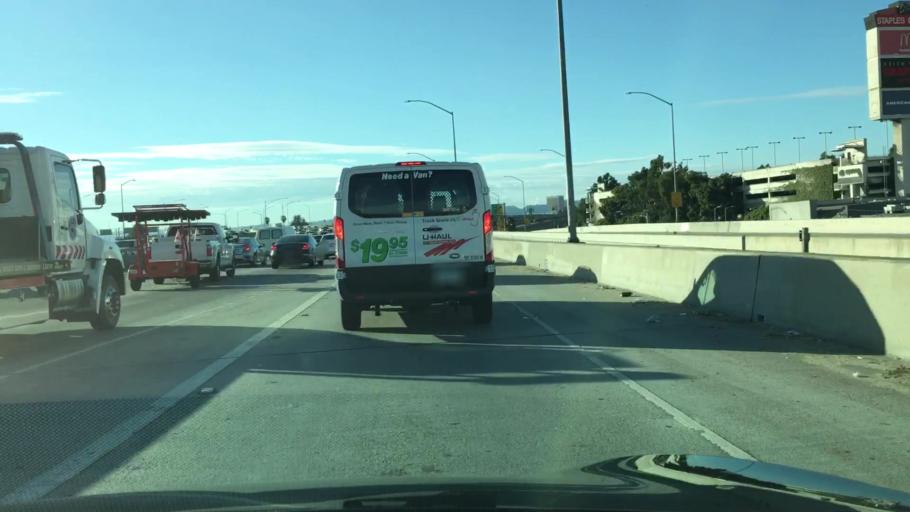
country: US
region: California
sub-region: Los Angeles County
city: Los Angeles
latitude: 34.0362
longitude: -118.2694
